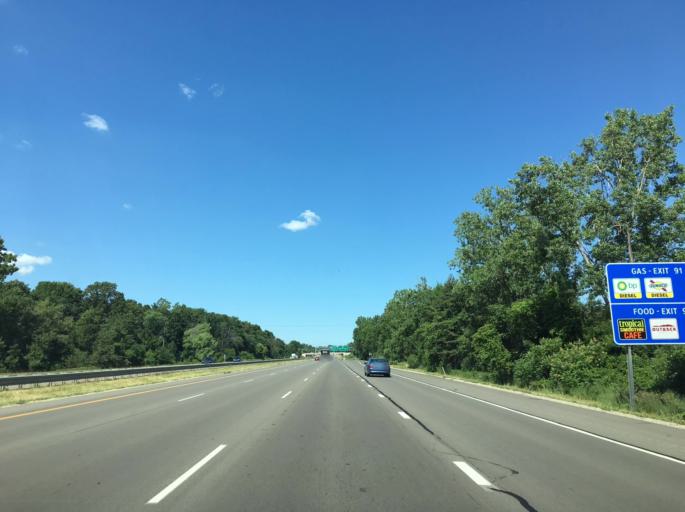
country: US
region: Michigan
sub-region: Oakland County
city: Clarkston
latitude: 42.7461
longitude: -83.4082
